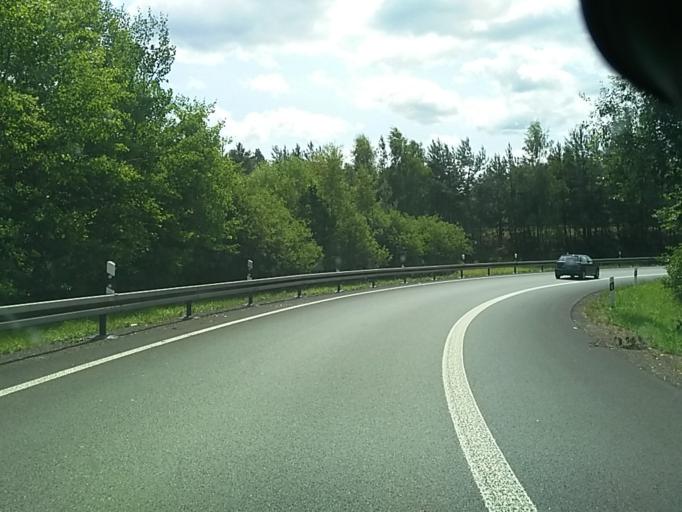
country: DE
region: Thuringia
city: Hermsdorf
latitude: 50.8801
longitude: 11.8489
